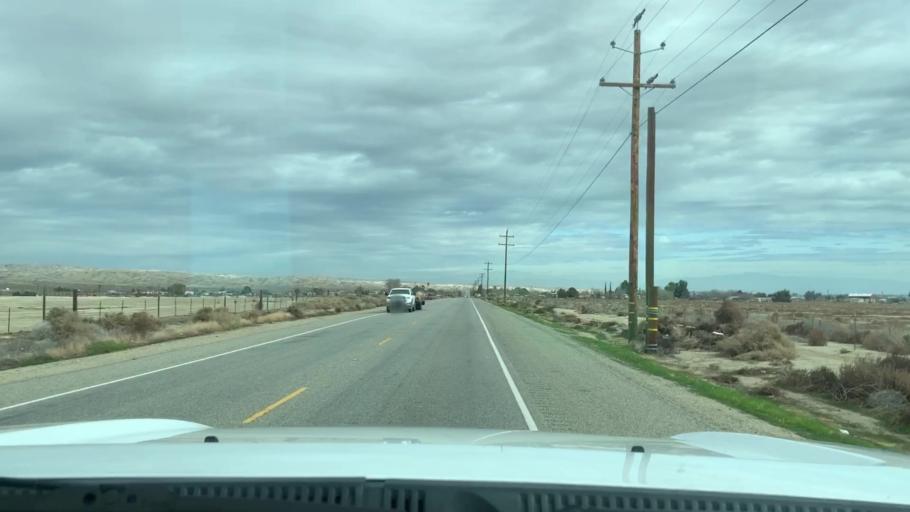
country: US
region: California
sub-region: Kern County
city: Ford City
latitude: 35.2136
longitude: -119.3991
